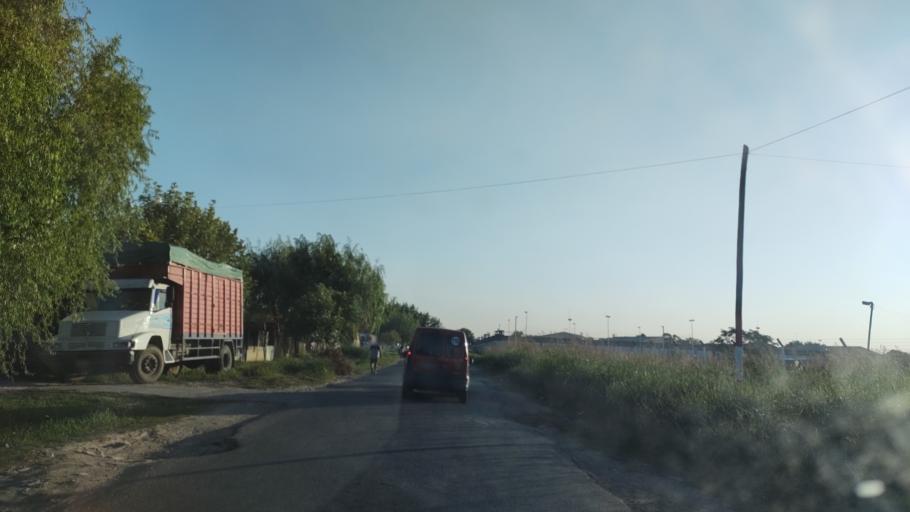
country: AR
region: Buenos Aires
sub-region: Partido de La Plata
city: La Plata
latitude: -34.9687
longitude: -57.9692
